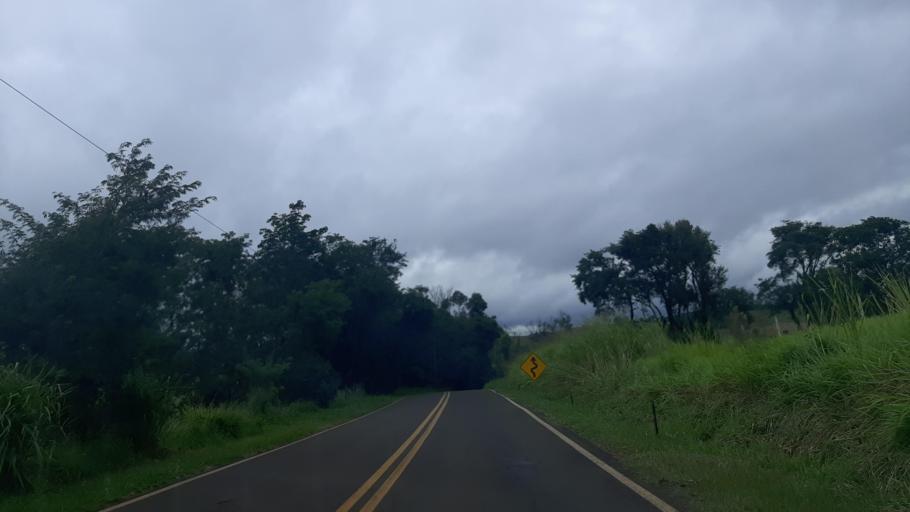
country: BR
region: Parana
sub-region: Ampere
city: Ampere
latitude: -25.9707
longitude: -53.4424
